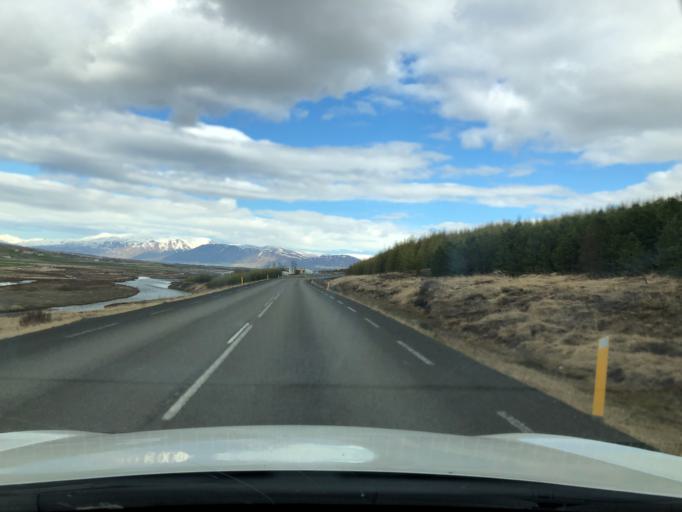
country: IS
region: Northeast
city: Akureyri
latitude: 65.7384
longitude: -18.2886
